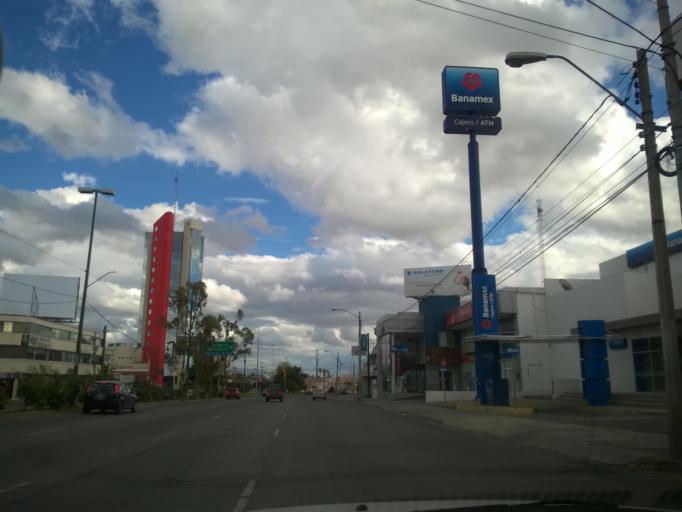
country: MX
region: Guanajuato
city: Leon
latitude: 21.1427
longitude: -101.6914
